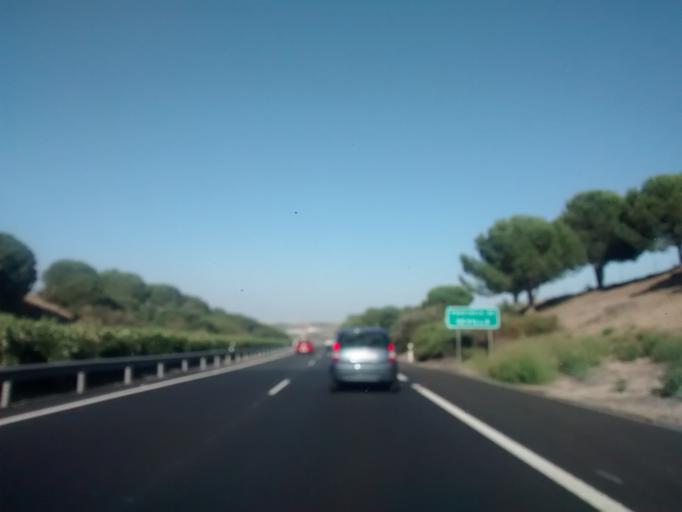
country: ES
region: Andalusia
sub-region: Provincia de Huelva
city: Chucena
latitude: 37.3539
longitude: -6.3648
